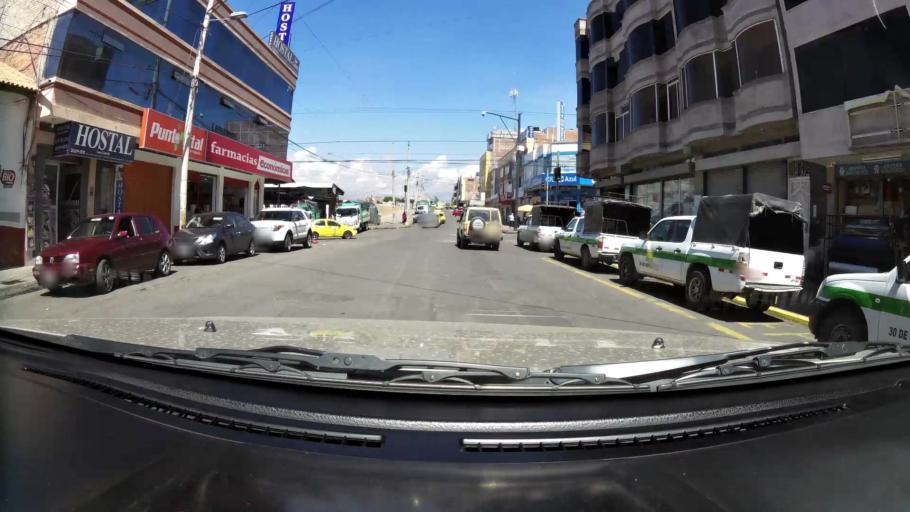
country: EC
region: Chimborazo
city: Riobamba
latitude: -1.6664
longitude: -78.6432
